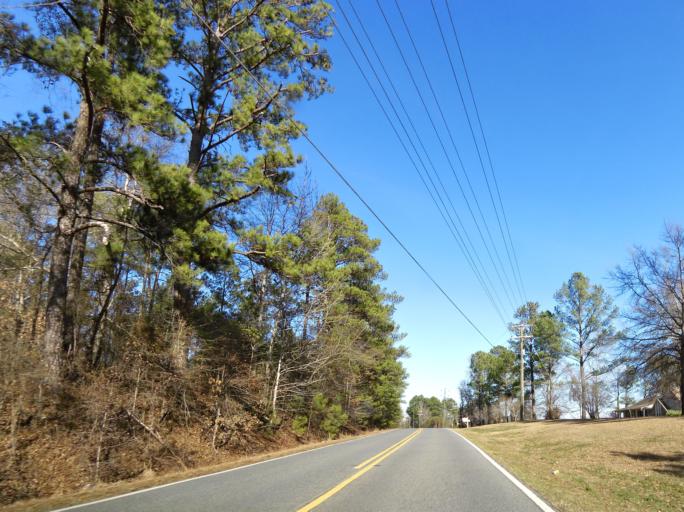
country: US
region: Georgia
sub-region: Bibb County
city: West Point
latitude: 32.7792
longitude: -83.8163
